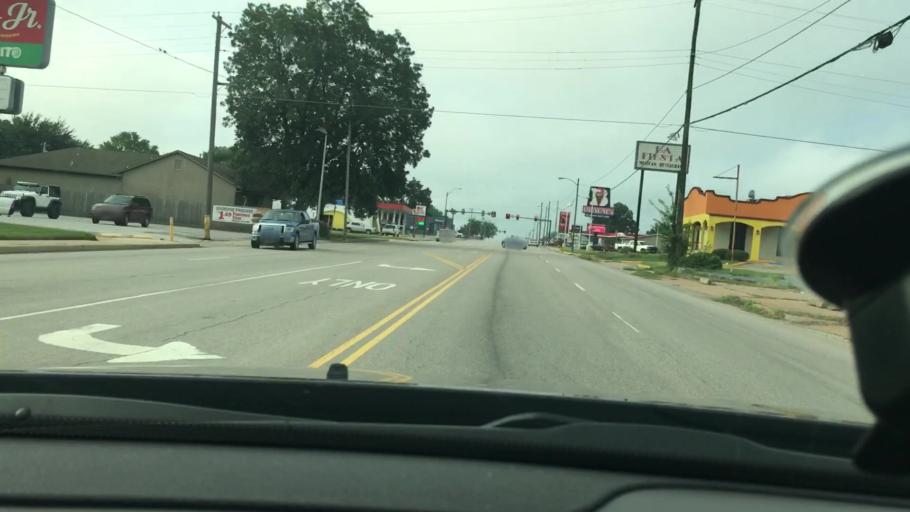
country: US
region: Oklahoma
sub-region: Pontotoc County
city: Ada
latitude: 34.7733
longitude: -96.6700
